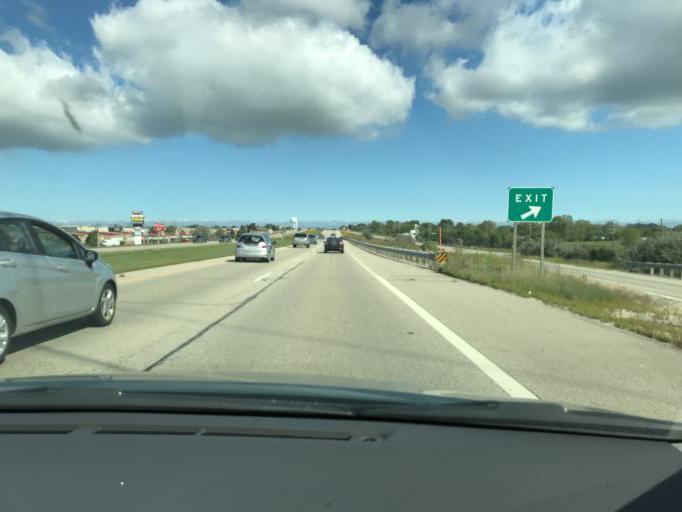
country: US
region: Wisconsin
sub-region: Kenosha County
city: Pleasant Prairie
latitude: 42.5666
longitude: -87.9041
